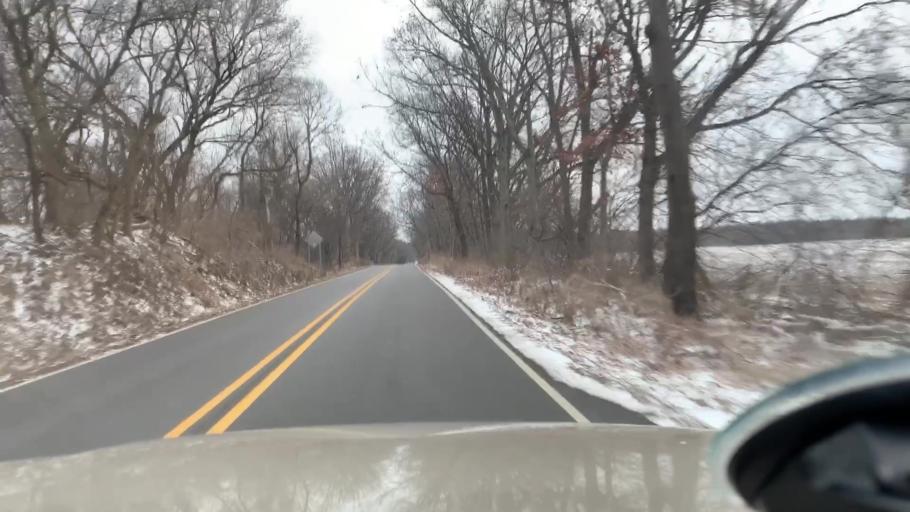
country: US
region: Michigan
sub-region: Jackson County
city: Spring Arbor
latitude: 42.2094
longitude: -84.5309
